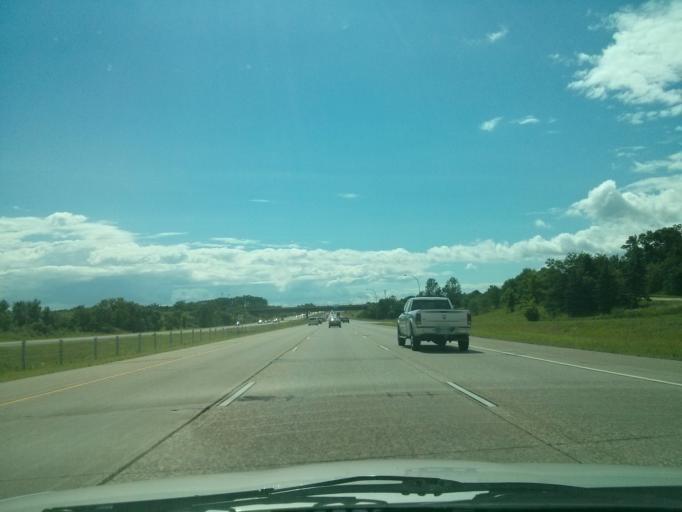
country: US
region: Minnesota
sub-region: Washington County
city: Lakeland
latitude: 44.9564
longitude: -92.7920
